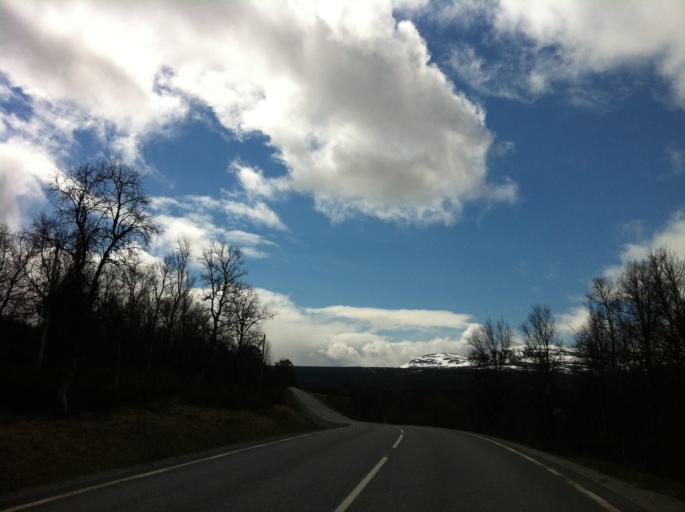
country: NO
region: Sor-Trondelag
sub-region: Tydal
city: Aas
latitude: 62.6569
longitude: 12.4276
